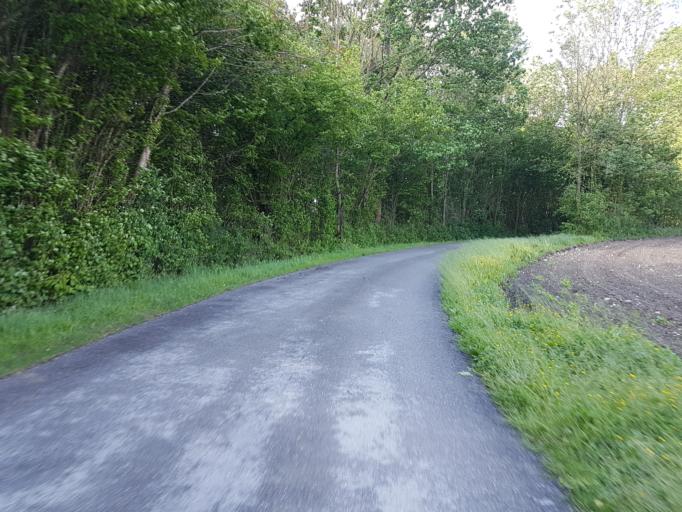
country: FR
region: Rhone-Alpes
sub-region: Departement de la Savoie
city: Chindrieux
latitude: 45.8835
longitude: 5.8359
